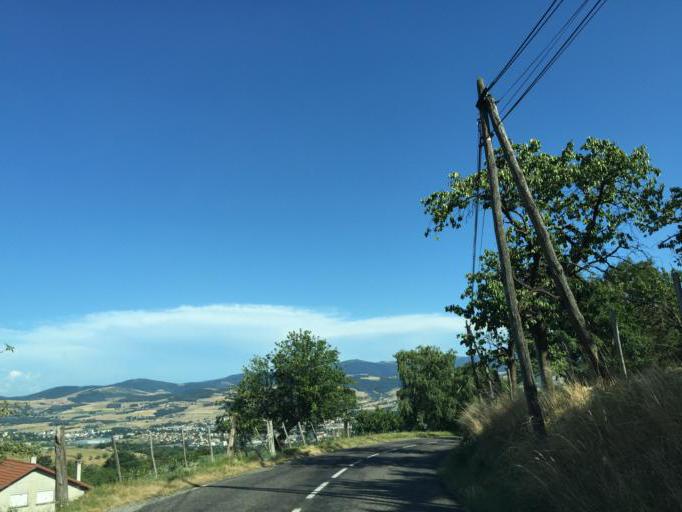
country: FR
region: Rhone-Alpes
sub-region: Departement de la Loire
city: Sorbiers
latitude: 45.4966
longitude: 4.4864
